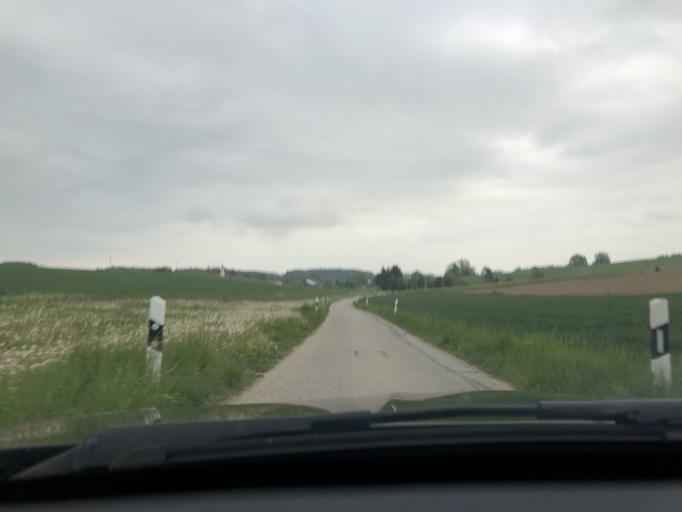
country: DE
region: Bavaria
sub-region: Upper Bavaria
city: Freising
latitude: 48.4287
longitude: 11.7363
